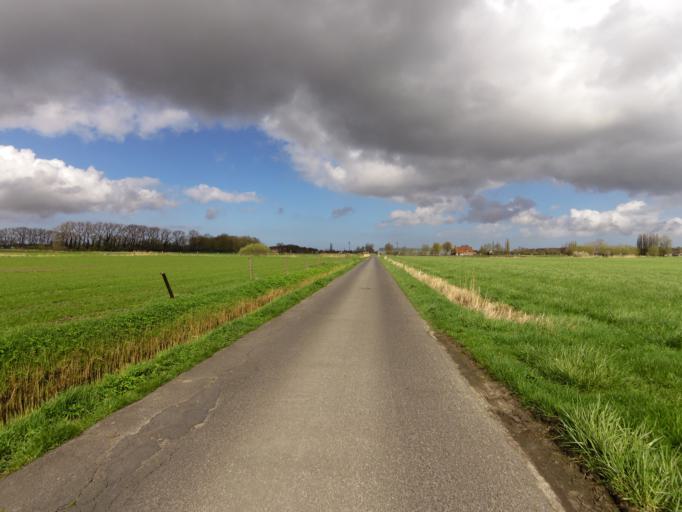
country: BE
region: Flanders
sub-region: Provincie West-Vlaanderen
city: Gistel
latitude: 51.1462
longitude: 2.9808
